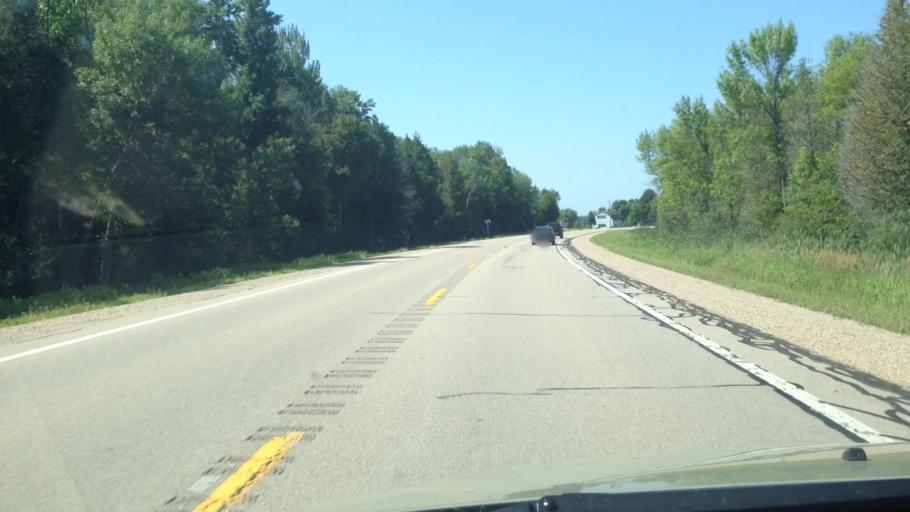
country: US
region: Michigan
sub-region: Menominee County
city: Menominee
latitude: 45.3801
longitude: -87.3772
